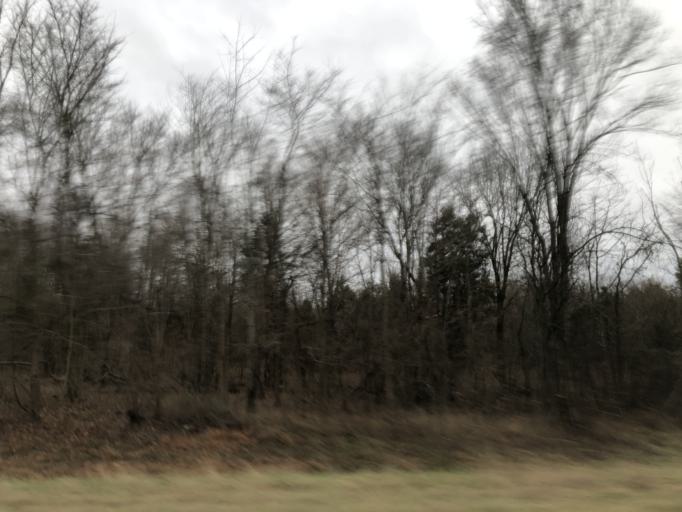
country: US
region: Illinois
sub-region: Johnson County
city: Vienna
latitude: 37.3832
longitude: -88.8257
